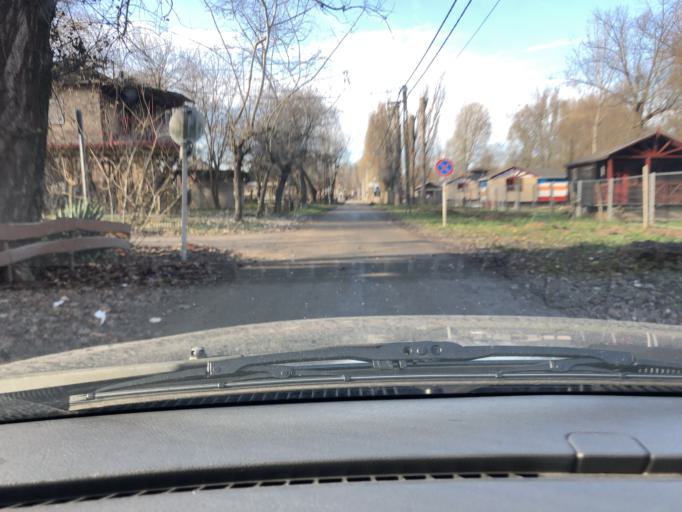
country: HU
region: Csongrad
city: Csongrad
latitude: 46.7146
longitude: 20.1867
